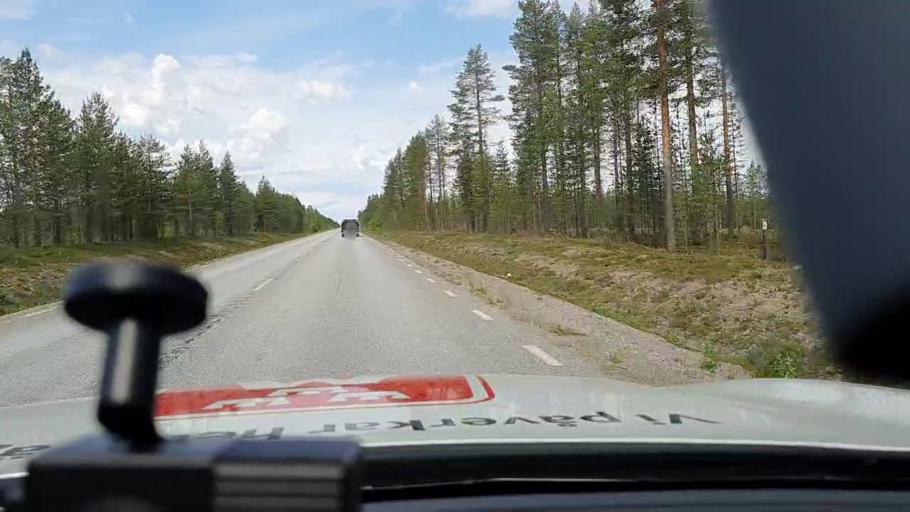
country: SE
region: Norrbotten
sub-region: Jokkmokks Kommun
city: Jokkmokk
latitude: 66.5208
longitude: 20.2138
